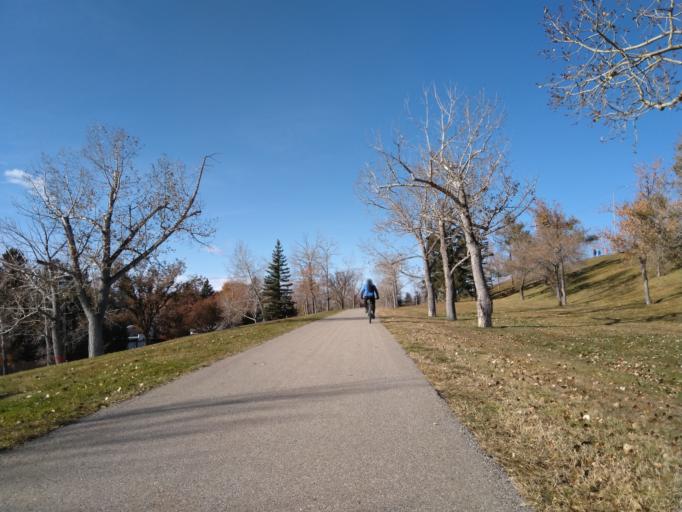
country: CA
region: Alberta
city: Calgary
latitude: 51.0936
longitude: -114.1125
